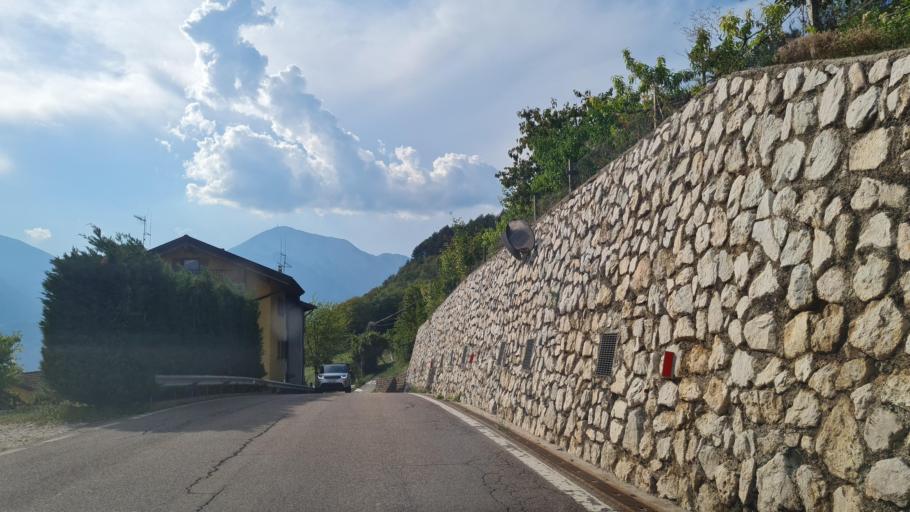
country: IT
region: Trentino-Alto Adige
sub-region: Provincia di Trento
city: Vigolo Vattaro
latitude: 46.0063
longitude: 11.1724
